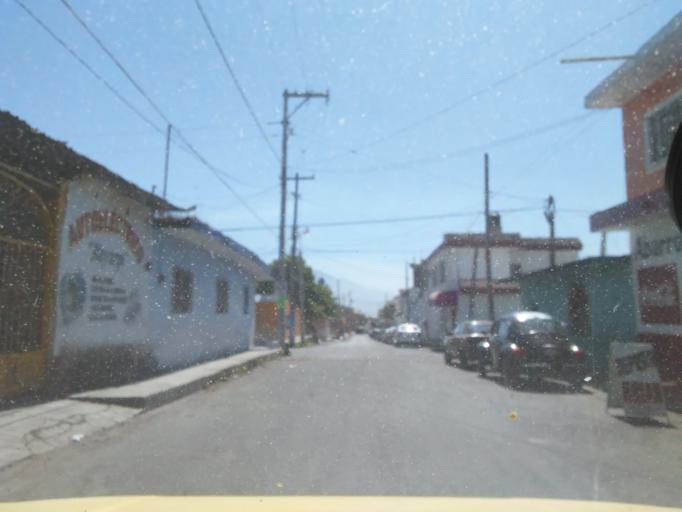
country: MX
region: Nayarit
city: Xalisco
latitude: 21.4484
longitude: -104.8973
